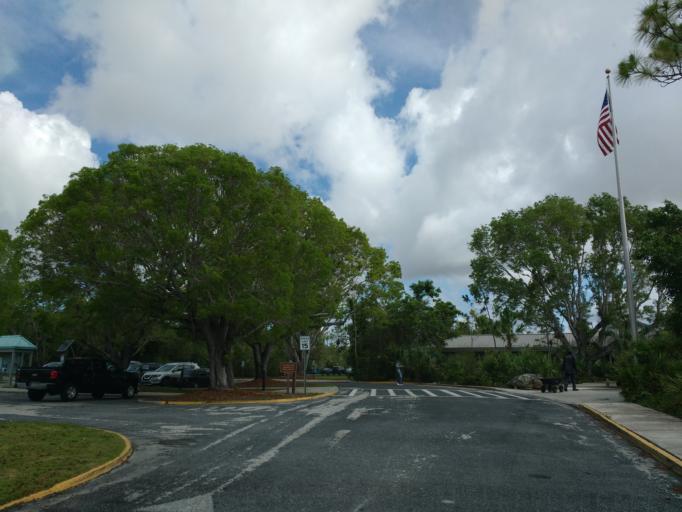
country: US
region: Florida
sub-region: Miami-Dade County
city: Florida City
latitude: 25.3950
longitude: -80.5837
